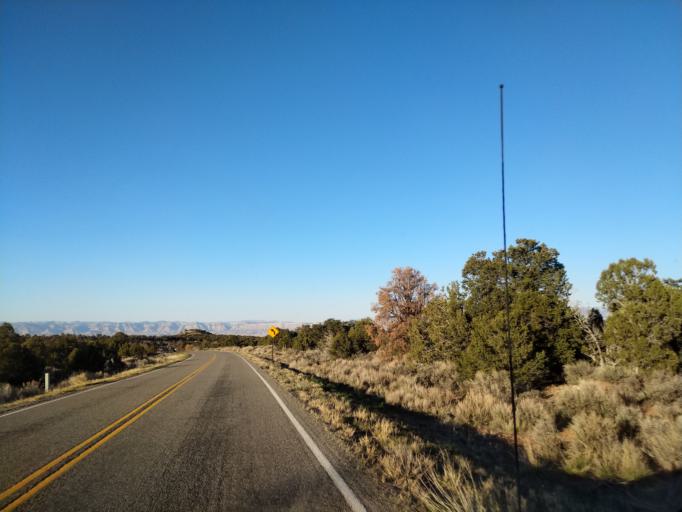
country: US
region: Colorado
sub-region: Mesa County
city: Redlands
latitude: 39.0116
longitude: -108.6729
